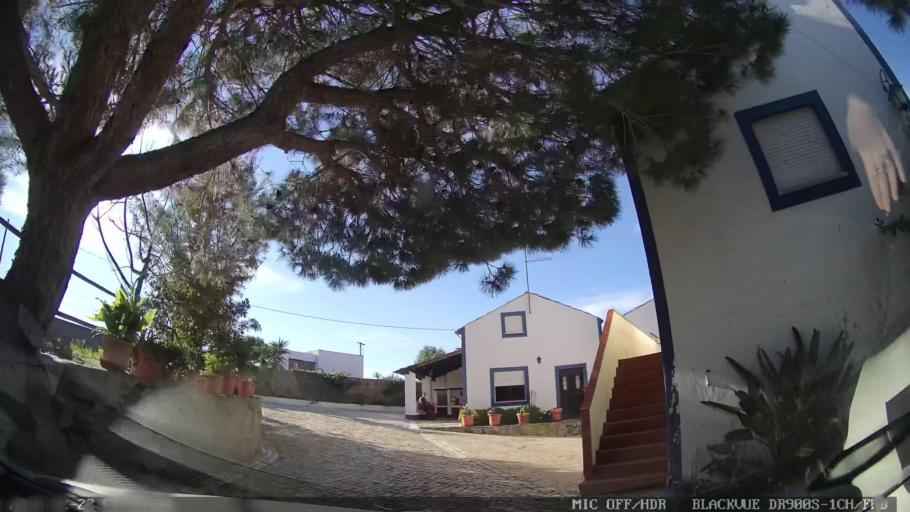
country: PT
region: Lisbon
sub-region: Vila Franca de Xira
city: Sao Joao dos Montes
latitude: 38.9717
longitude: -9.0192
